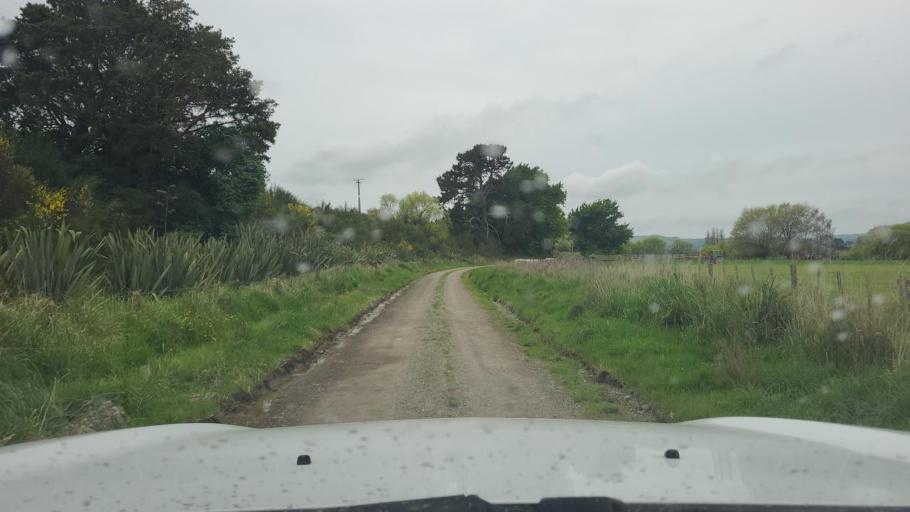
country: NZ
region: Wellington
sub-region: Masterton District
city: Masterton
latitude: -41.0729
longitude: 175.6233
